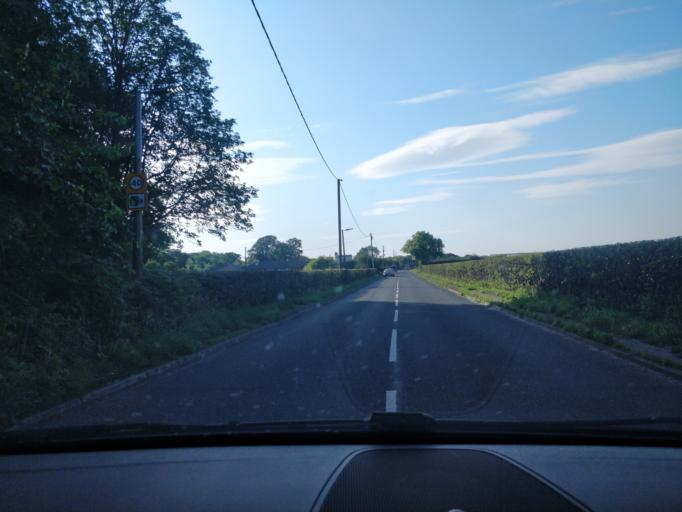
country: GB
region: England
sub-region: Lancashire
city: Tarleton
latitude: 53.6486
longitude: -2.8725
